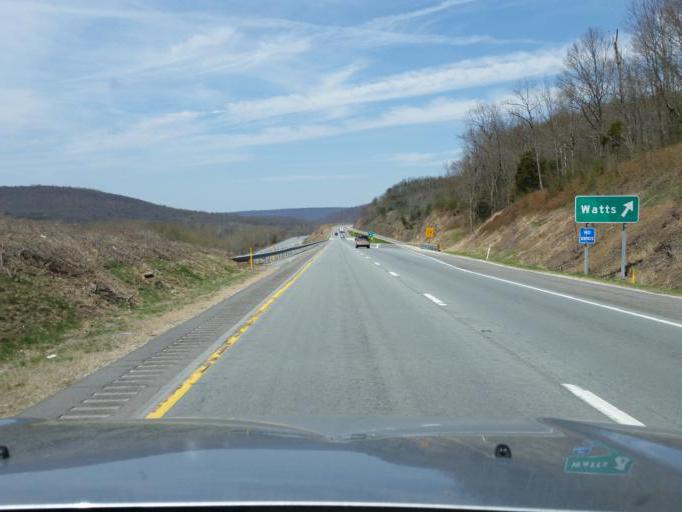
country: US
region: Pennsylvania
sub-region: Perry County
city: Duncannon
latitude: 40.4474
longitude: -77.0188
